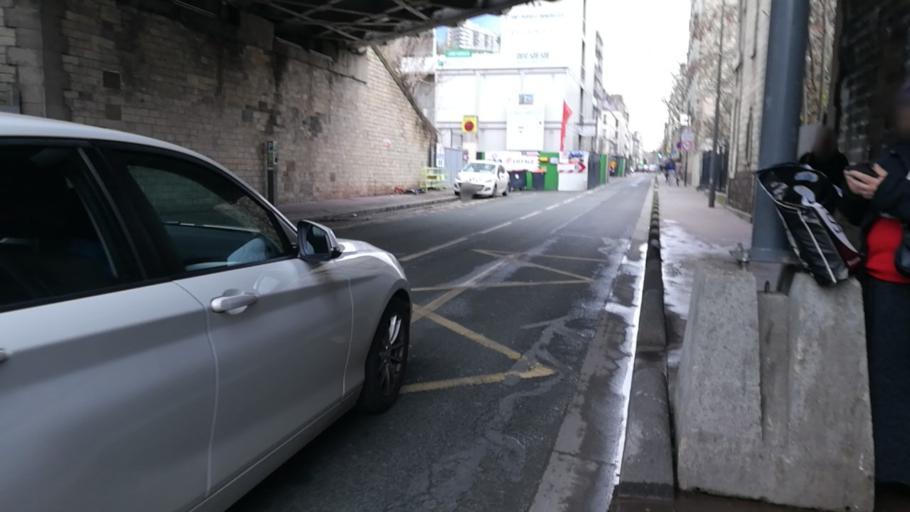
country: FR
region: Ile-de-France
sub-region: Paris
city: Saint-Ouen
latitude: 48.9078
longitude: 2.3335
